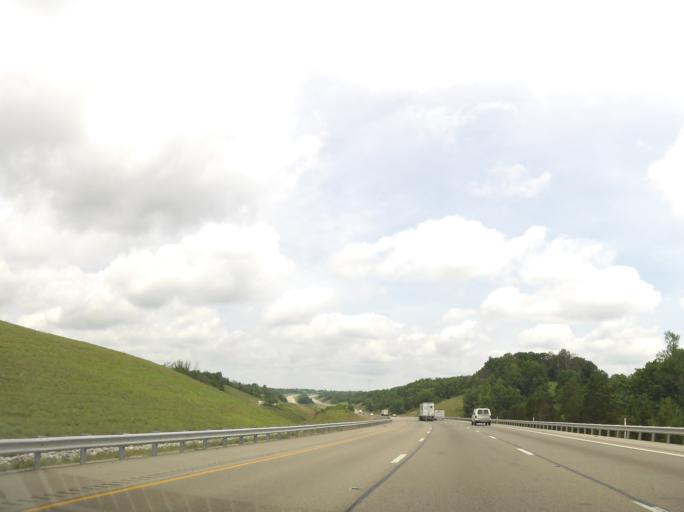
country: US
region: Kentucky
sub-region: Grant County
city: Williamstown
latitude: 38.5274
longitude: -84.5866
